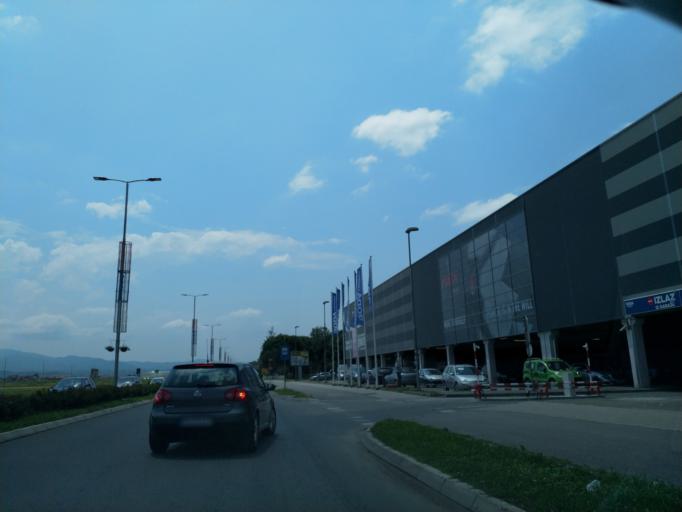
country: RS
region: Central Serbia
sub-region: Rasinski Okrug
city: Krusevac
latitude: 43.5686
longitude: 21.3369
